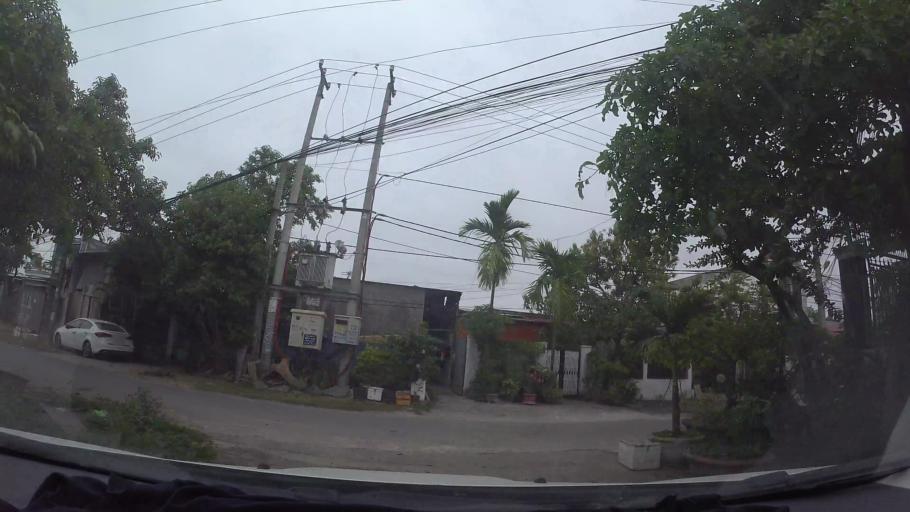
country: VN
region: Da Nang
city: Lien Chieu
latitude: 16.0648
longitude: 108.1483
